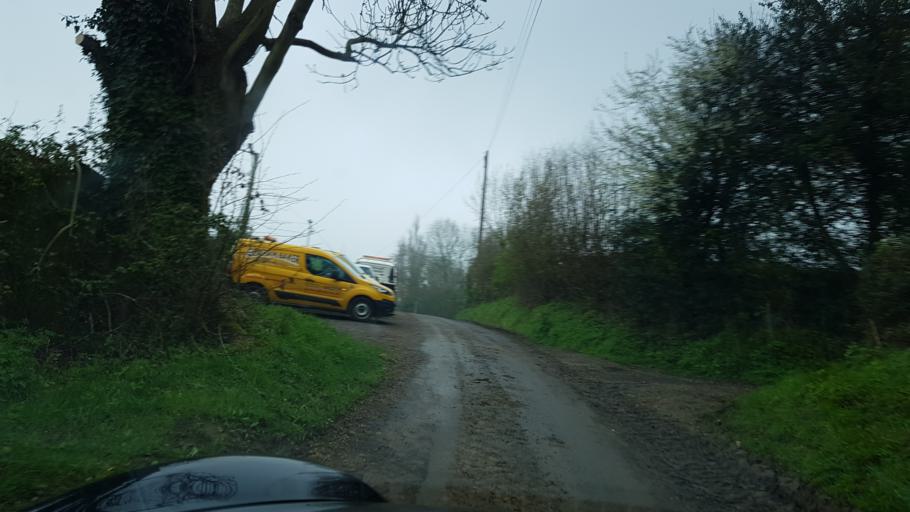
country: GB
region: England
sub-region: Herefordshire
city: Yatton
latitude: 52.0125
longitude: -2.5267
